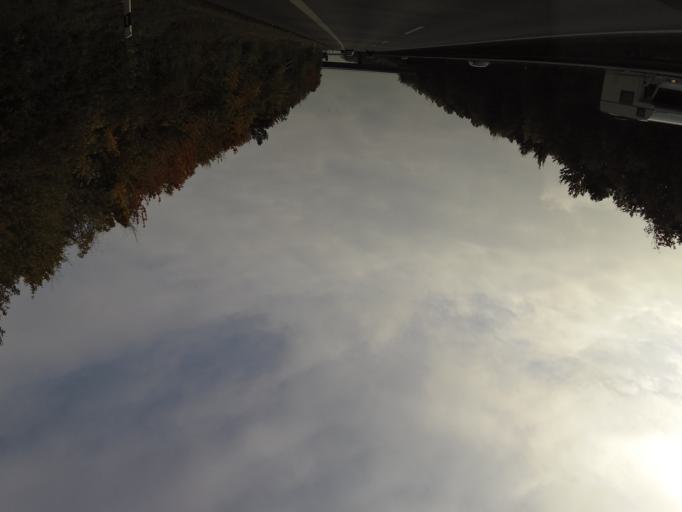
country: DE
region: Rheinland-Pfalz
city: Freimersheim
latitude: 49.7191
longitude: 8.0763
